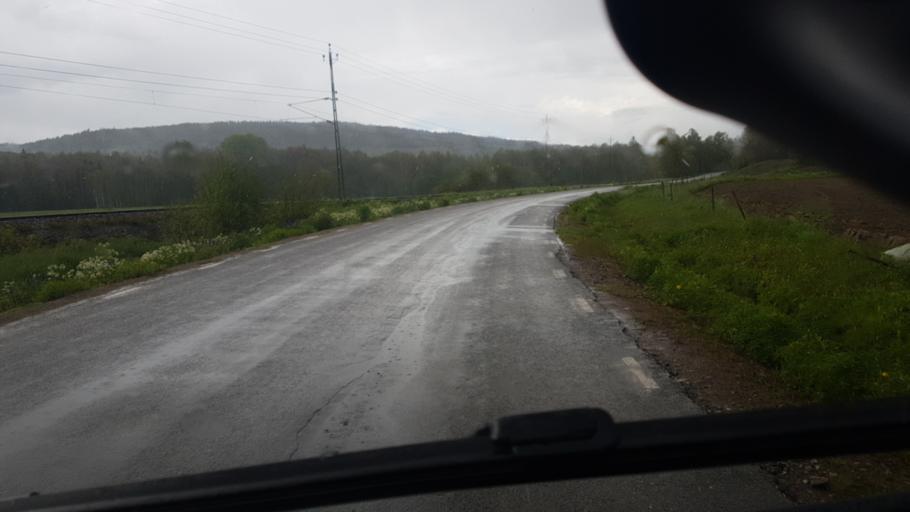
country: SE
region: Vaermland
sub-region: Eda Kommun
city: Amotfors
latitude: 59.7104
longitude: 12.4453
